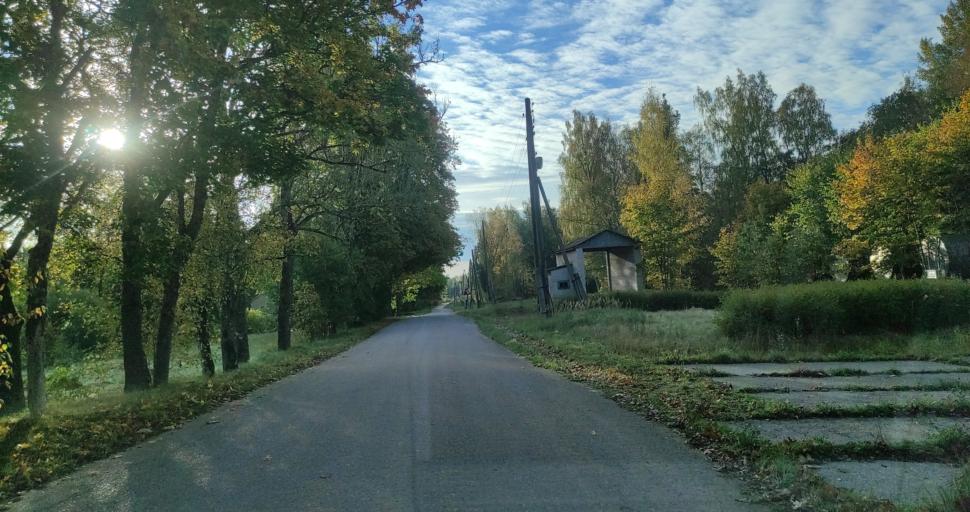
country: LV
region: Skrunda
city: Skrunda
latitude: 56.7421
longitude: 21.8803
